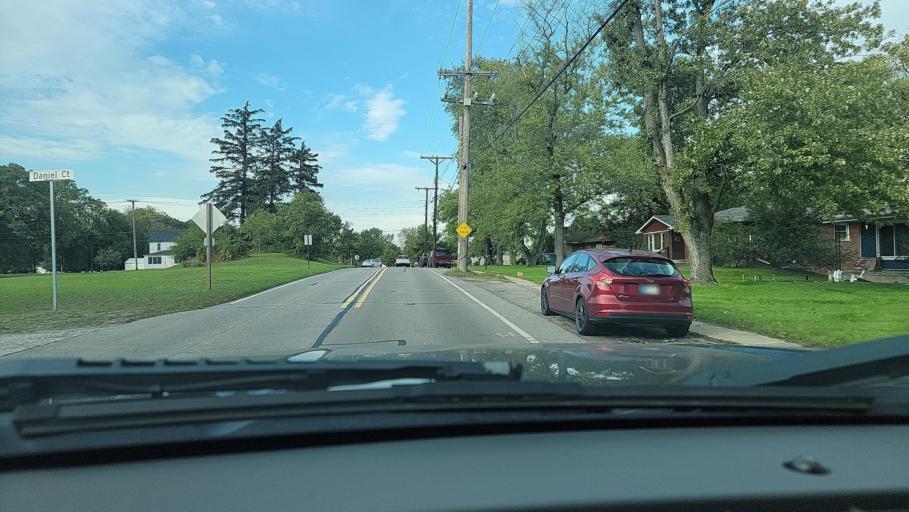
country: US
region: Indiana
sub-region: Porter County
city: Portage
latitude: 41.5860
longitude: -87.1688
